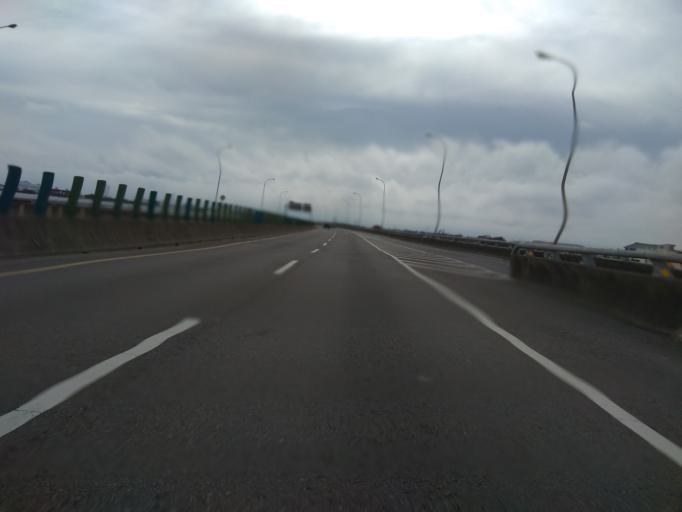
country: TW
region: Taiwan
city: Daxi
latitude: 24.9031
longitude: 121.2345
